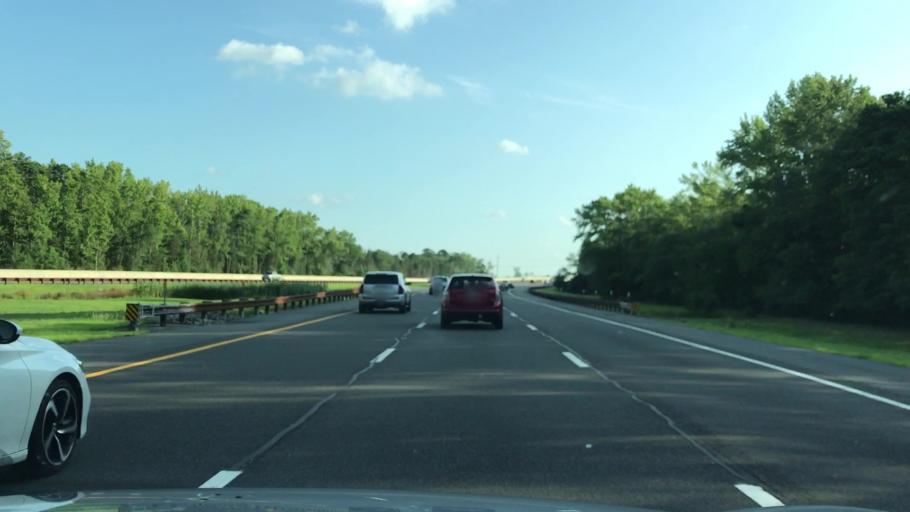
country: US
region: New Jersey
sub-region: Ocean County
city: Mystic Island
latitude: 39.5993
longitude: -74.4390
